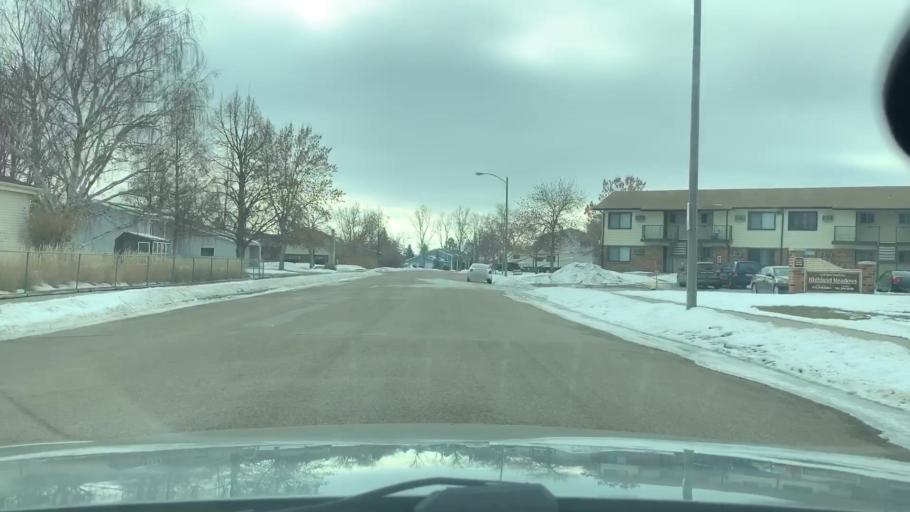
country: US
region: North Dakota
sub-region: Burleigh County
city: Bismarck
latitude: 46.8272
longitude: -100.8067
